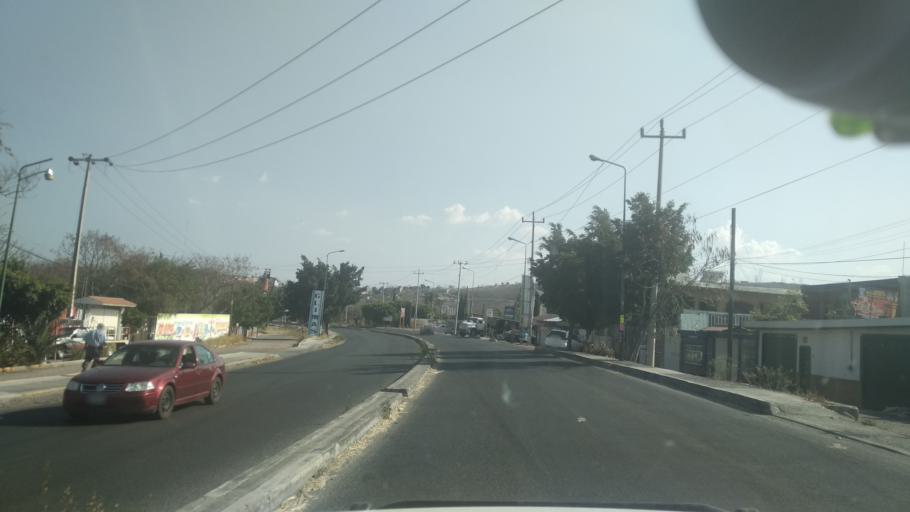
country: MX
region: Puebla
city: Izucar de Matamoros
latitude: 18.6213
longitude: -98.4710
